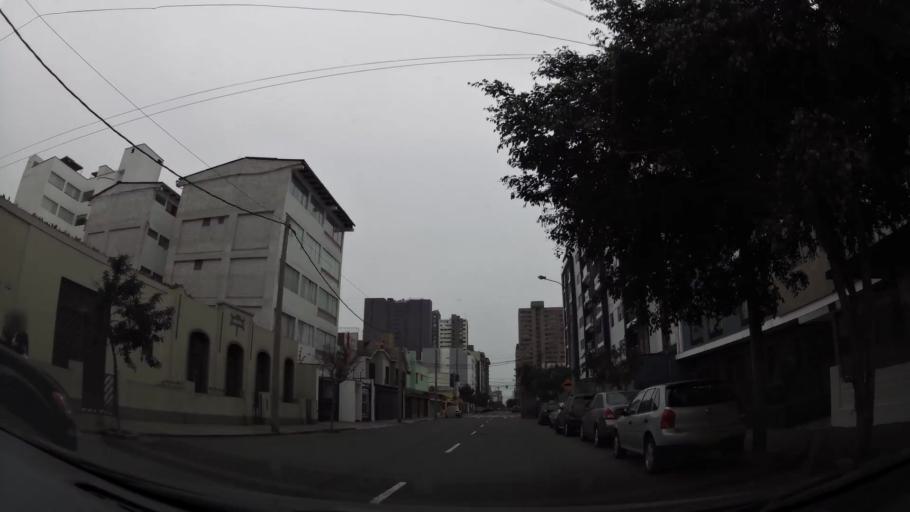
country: PE
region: Lima
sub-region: Lima
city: San Isidro
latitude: -12.1163
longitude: -77.0348
